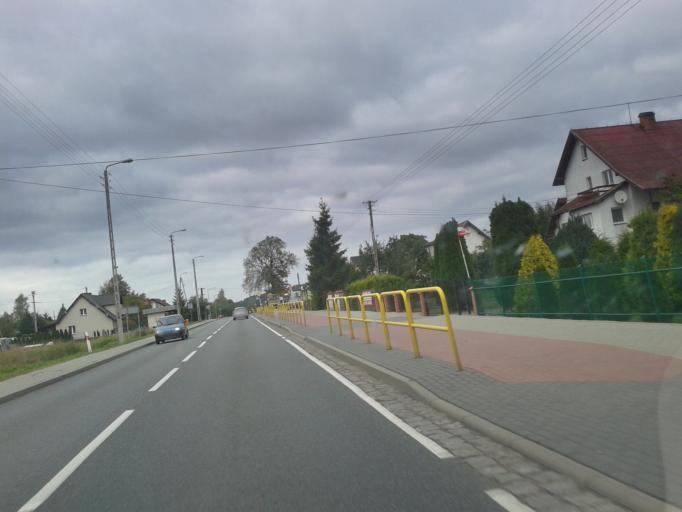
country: PL
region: Kujawsko-Pomorskie
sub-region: Powiat sepolenski
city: Sepolno Krajenskie
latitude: 53.4637
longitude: 17.5303
